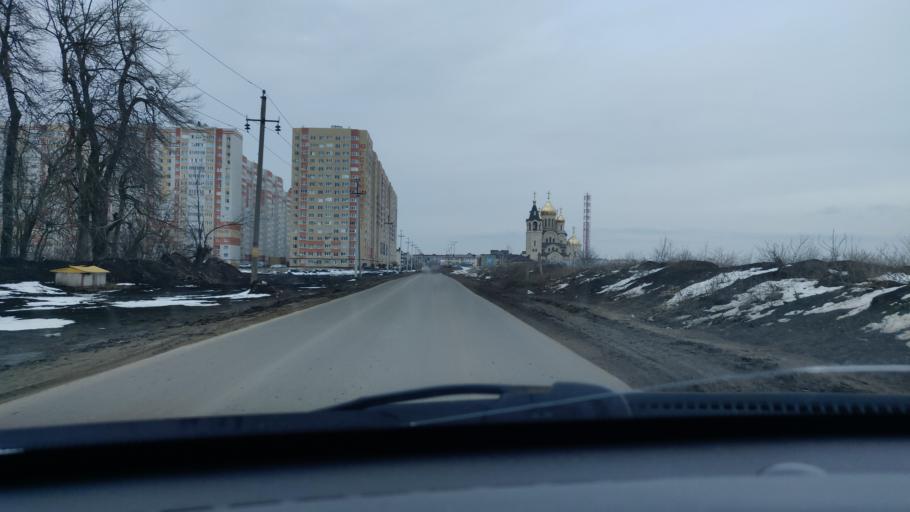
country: RU
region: Stavropol'skiy
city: Tatarka
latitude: 45.0105
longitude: 41.8972
